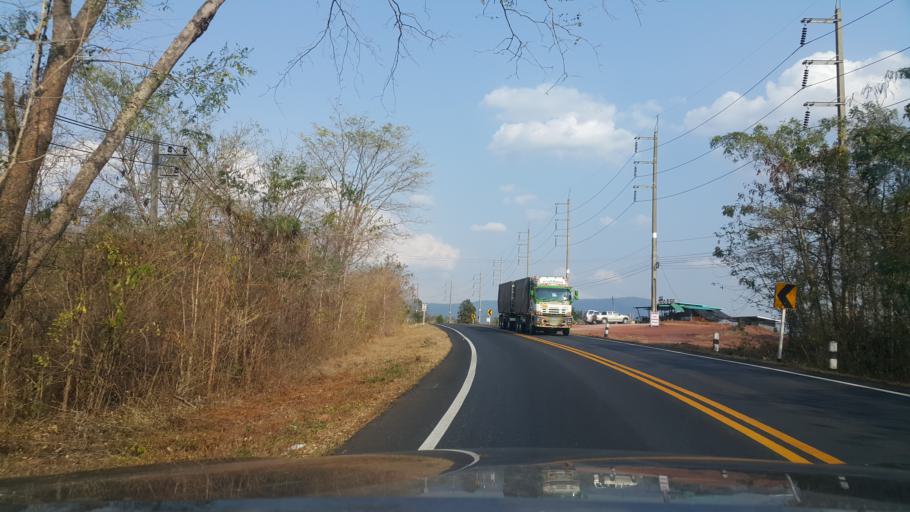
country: TH
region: Loei
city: Dan Sai
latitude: 17.1841
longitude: 100.9988
